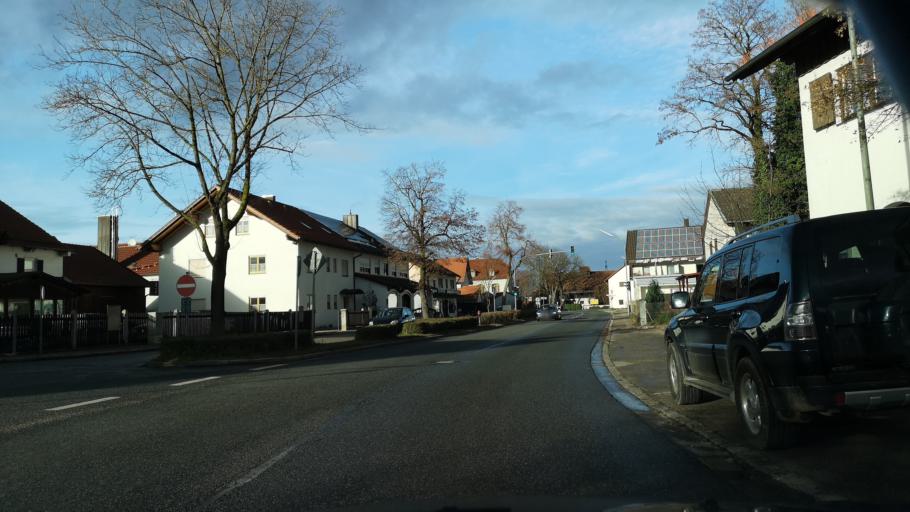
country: DE
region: Bavaria
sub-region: Upper Bavaria
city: Pliening
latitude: 48.1967
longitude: 11.7987
